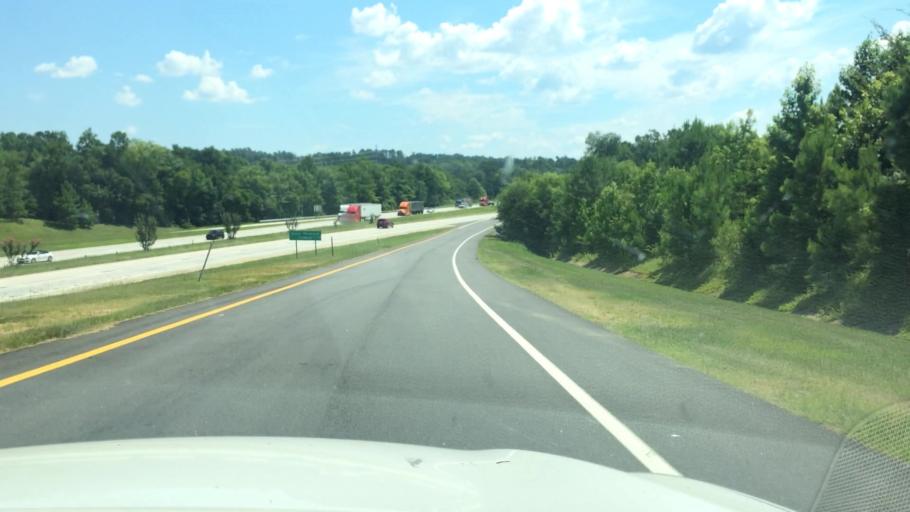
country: US
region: South Carolina
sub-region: Aiken County
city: North Augusta
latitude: 33.5402
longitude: -81.9897
